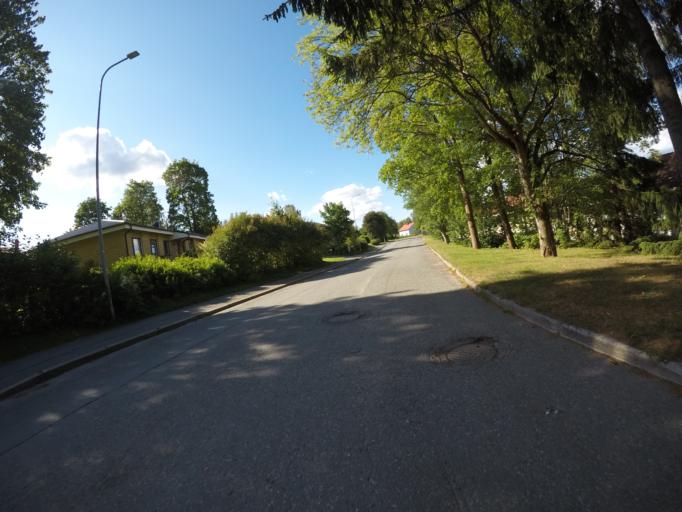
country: FI
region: Haeme
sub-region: Haemeenlinna
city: Haemeenlinna
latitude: 61.0054
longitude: 24.4982
